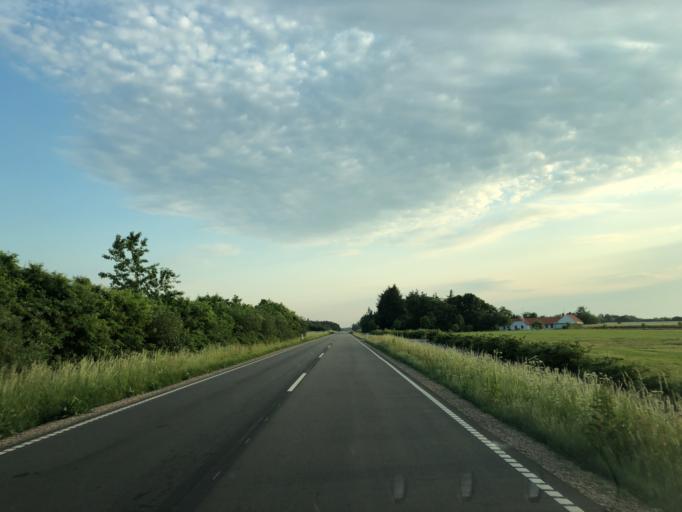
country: DK
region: Central Jutland
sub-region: Holstebro Kommune
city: Ulfborg
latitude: 56.3534
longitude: 8.3739
